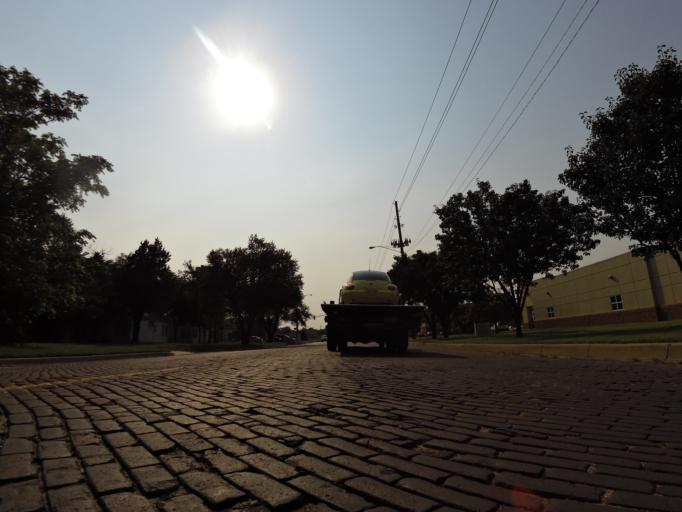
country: US
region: Kansas
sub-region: Sedgwick County
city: Wichita
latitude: 37.7009
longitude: -97.3071
